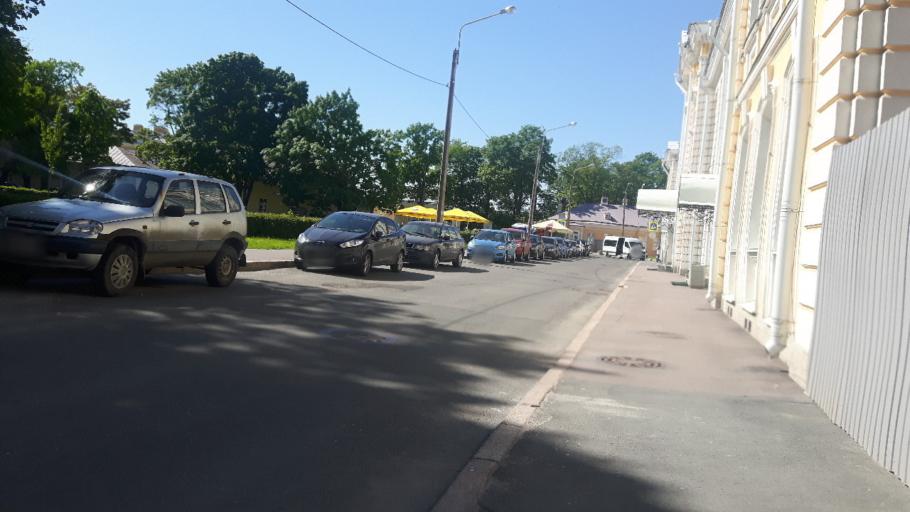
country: RU
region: St.-Petersburg
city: Peterhof
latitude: 59.8831
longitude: 29.9135
